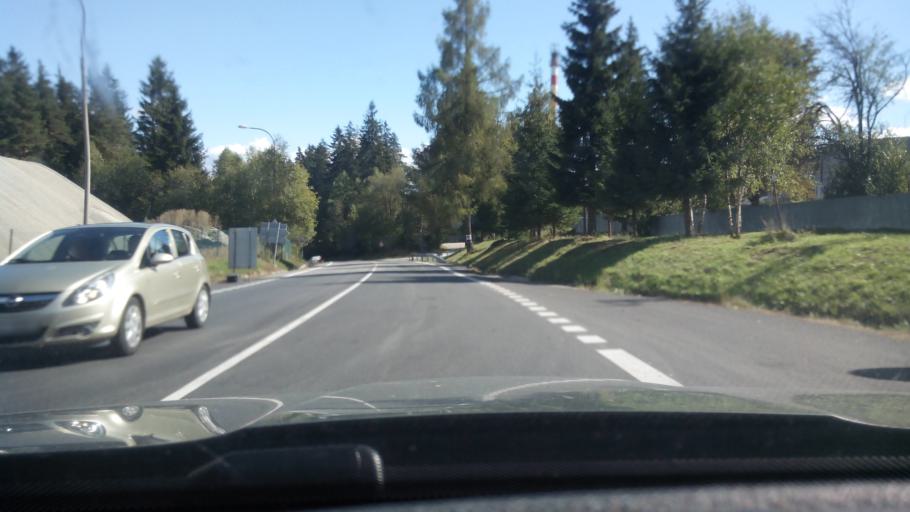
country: CZ
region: Jihocesky
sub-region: Okres Prachatice
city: Vimperk
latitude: 49.0629
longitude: 13.7381
